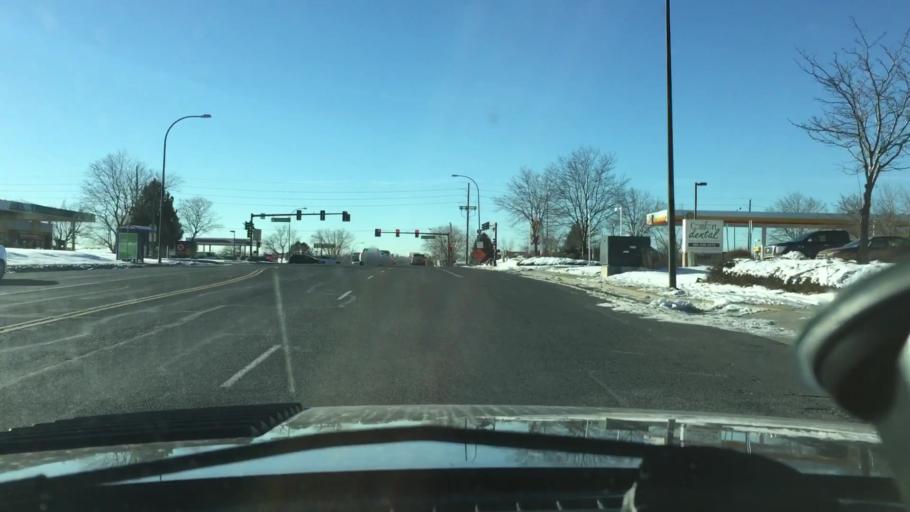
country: US
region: Colorado
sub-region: Adams County
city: Federal Heights
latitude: 39.8647
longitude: -104.9967
